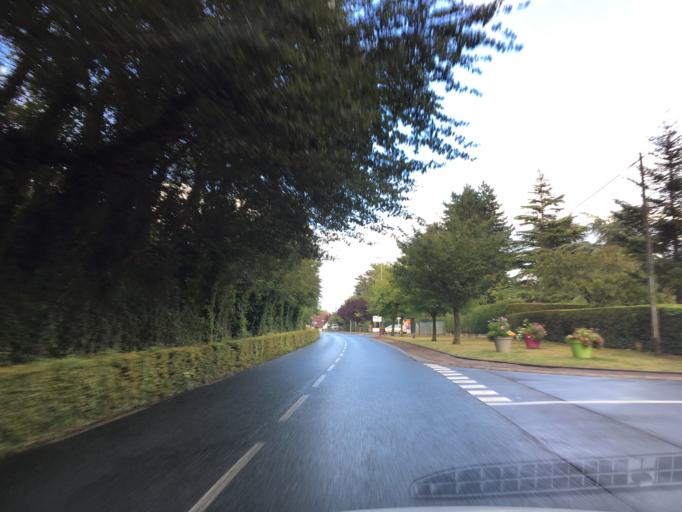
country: FR
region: Lower Normandy
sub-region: Departement du Calvados
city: Merville-Franceville-Plage
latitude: 49.2758
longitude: -0.2090
